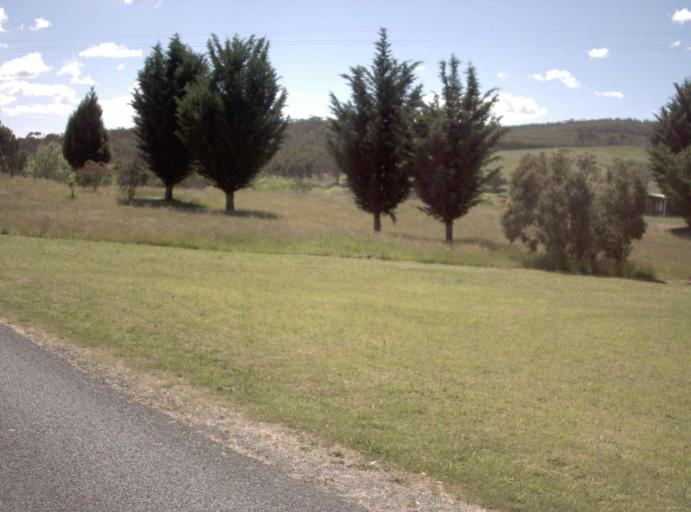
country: AU
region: New South Wales
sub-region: Bombala
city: Bombala
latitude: -37.0488
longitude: 148.8111
